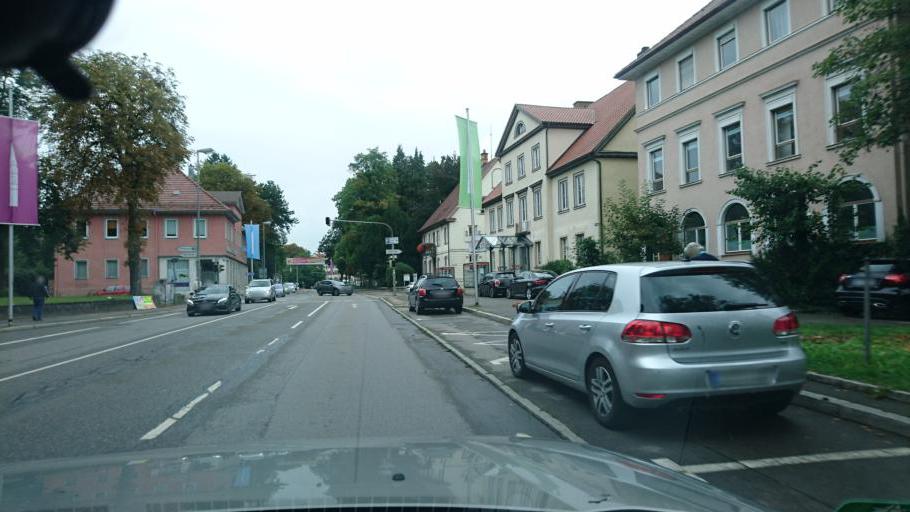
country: DE
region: Baden-Wuerttemberg
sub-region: Freiburg Region
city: Rottweil
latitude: 48.1641
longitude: 8.6297
